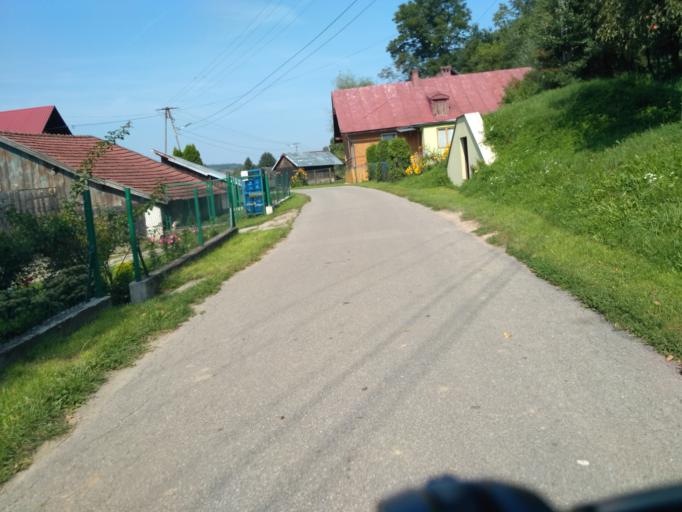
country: PL
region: Subcarpathian Voivodeship
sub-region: Powiat strzyzowski
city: Jawornik
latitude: 49.8227
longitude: 21.8391
